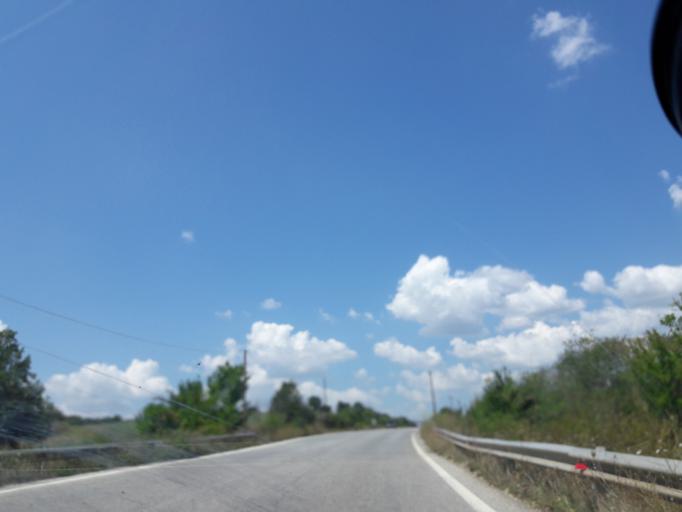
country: GR
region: Central Macedonia
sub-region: Nomos Chalkidikis
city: Galatista
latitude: 40.4614
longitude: 23.3783
